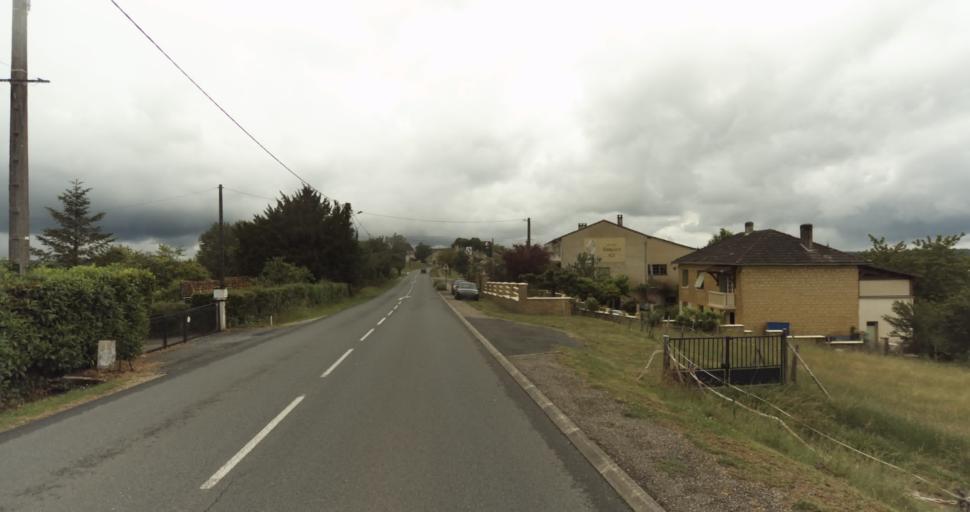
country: FR
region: Aquitaine
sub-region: Departement de la Dordogne
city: Beaumont-du-Perigord
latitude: 44.7633
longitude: 0.7698
